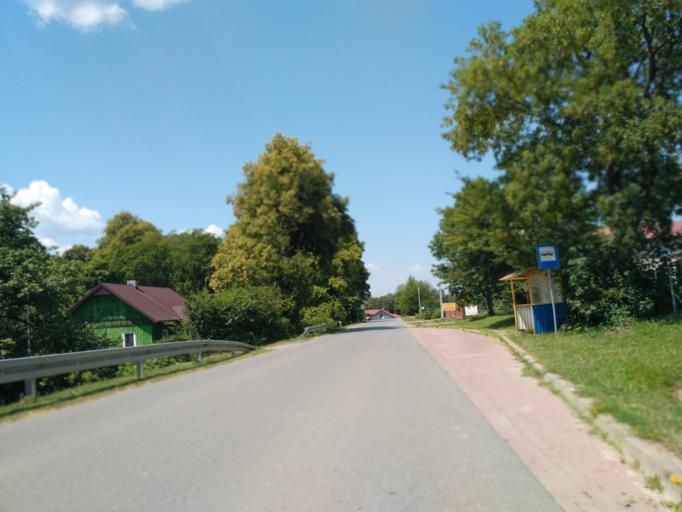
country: PL
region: Subcarpathian Voivodeship
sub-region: Powiat sanocki
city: Niebieszczany
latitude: 49.5092
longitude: 22.1522
